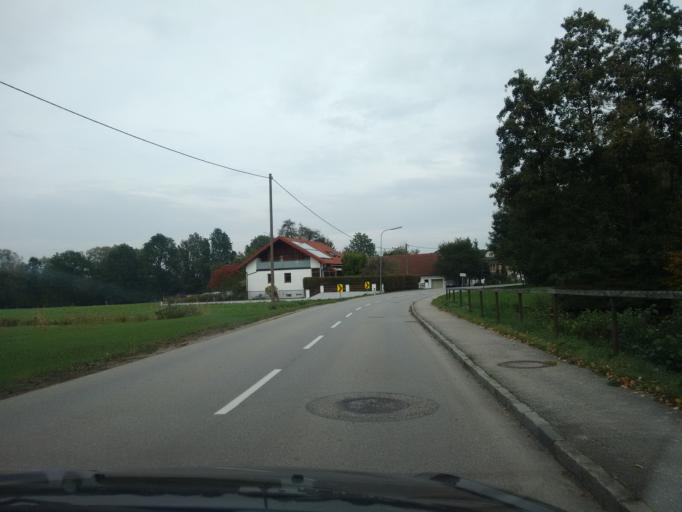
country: AT
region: Upper Austria
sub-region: Politischer Bezirk Grieskirchen
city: Bad Schallerbach
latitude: 48.1807
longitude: 13.8879
